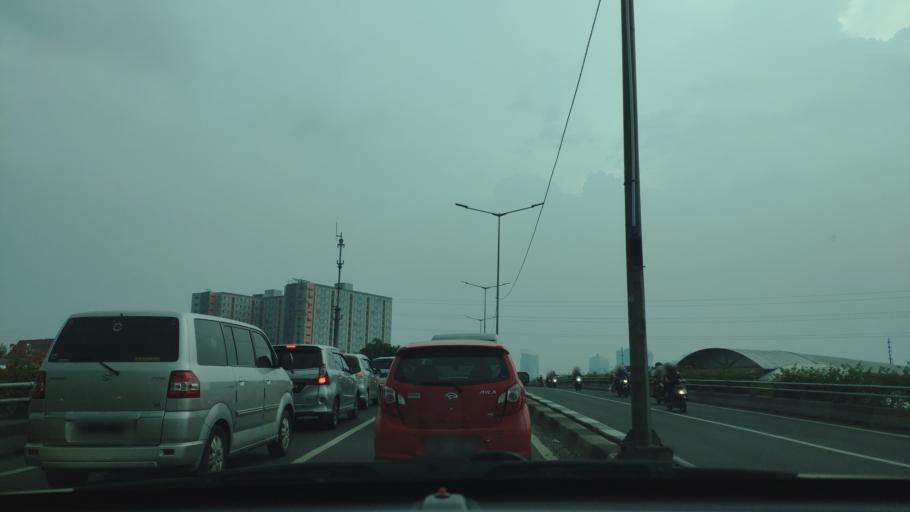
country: ID
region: Jakarta Raya
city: Jakarta
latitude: -6.1842
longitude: 106.8115
